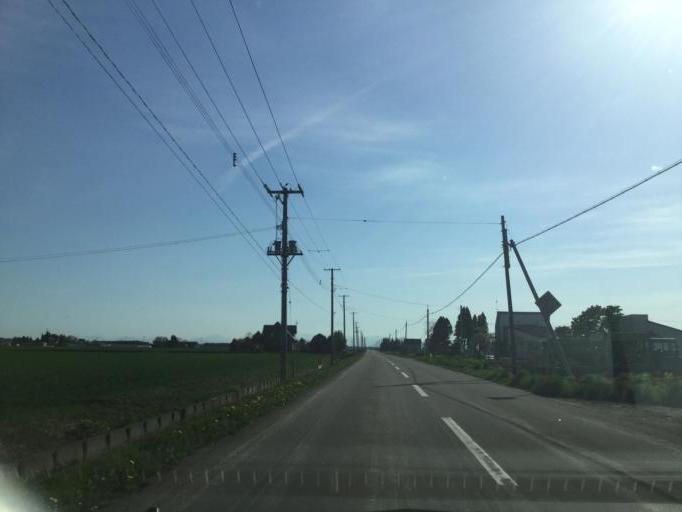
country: JP
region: Hokkaido
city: Iwamizawa
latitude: 43.1668
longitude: 141.7347
